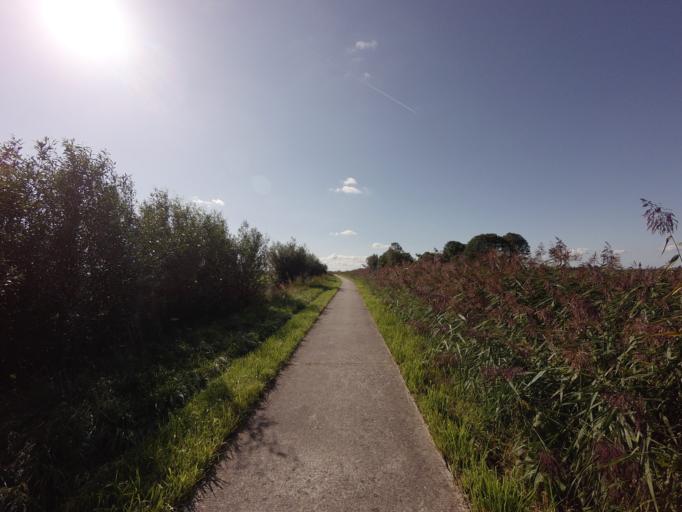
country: NL
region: Friesland
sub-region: Gemeente Boarnsterhim
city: Reduzum
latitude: 53.1296
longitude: 5.7559
